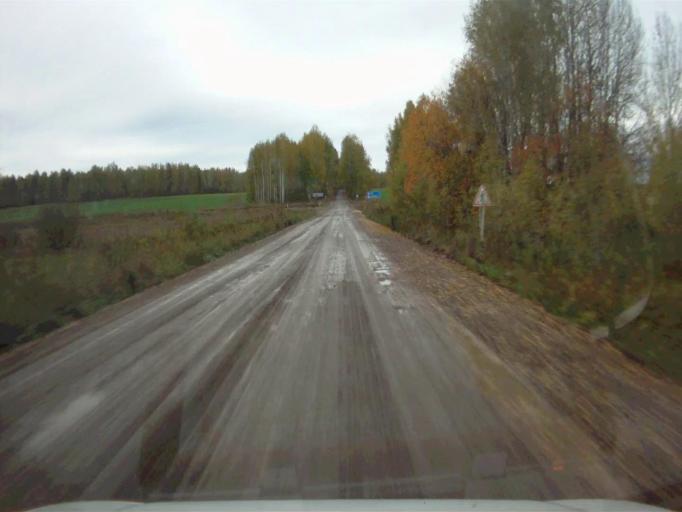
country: RU
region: Sverdlovsk
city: Mikhaylovsk
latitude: 56.1687
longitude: 59.2281
